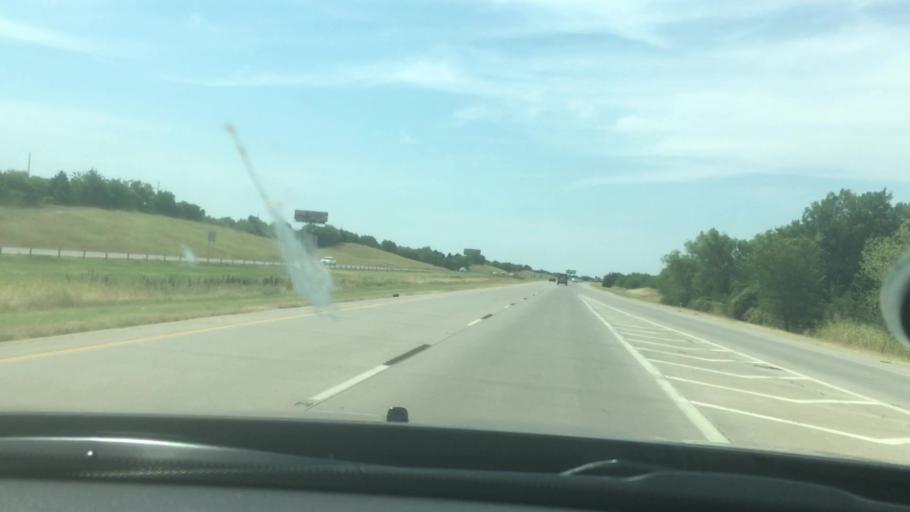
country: US
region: Oklahoma
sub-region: Carter County
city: Ardmore
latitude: 34.3007
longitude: -97.1599
